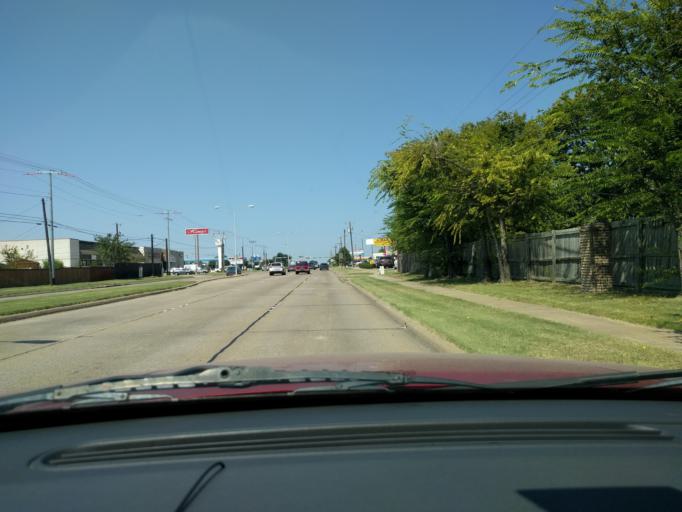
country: US
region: Texas
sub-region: Dallas County
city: Richardson
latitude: 32.9288
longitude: -96.7000
